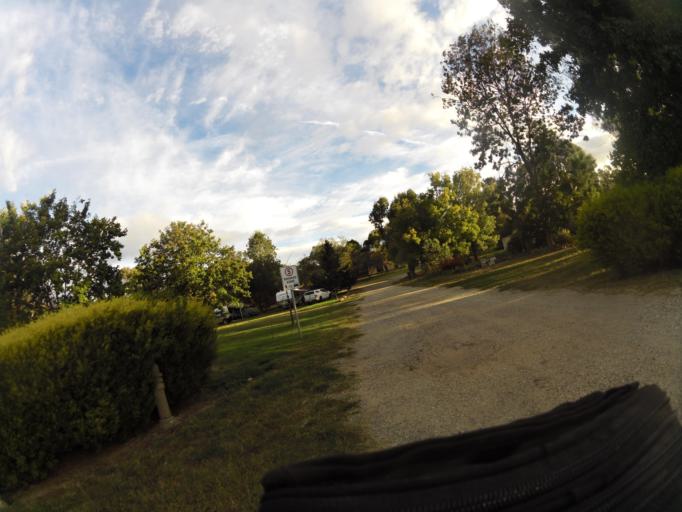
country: AU
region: New South Wales
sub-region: Greater Hume Shire
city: Holbrook
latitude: -36.0463
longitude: 147.9292
